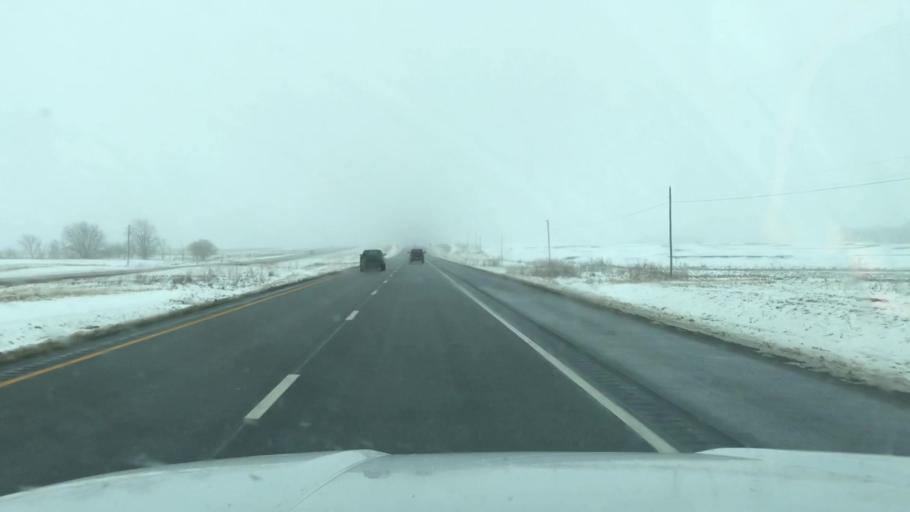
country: US
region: Missouri
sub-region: DeKalb County
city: Maysville
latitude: 39.7615
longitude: -94.3741
